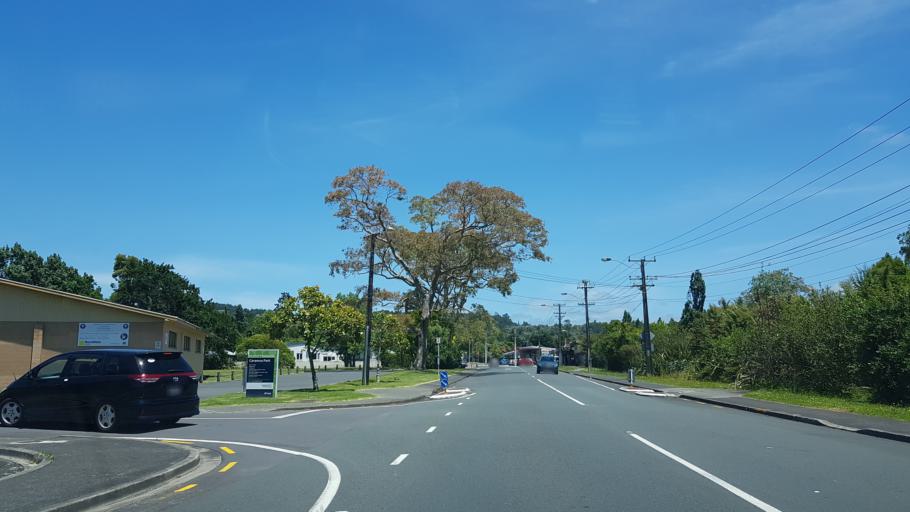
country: NZ
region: Auckland
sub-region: Auckland
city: Waitakere
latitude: -36.9203
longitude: 174.6493
